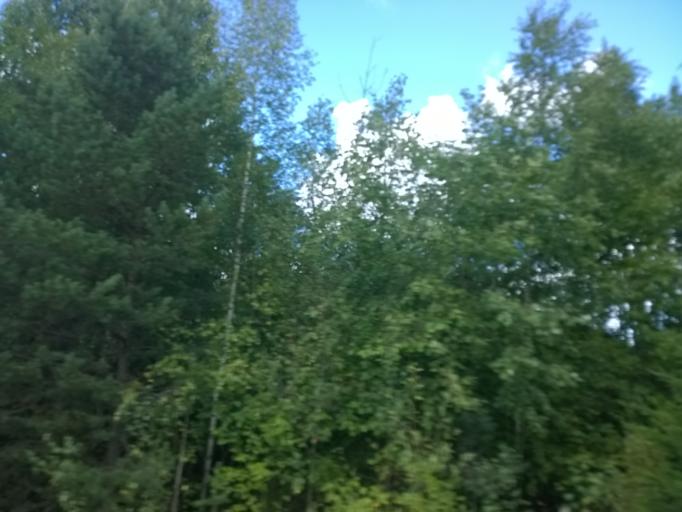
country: FI
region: Pirkanmaa
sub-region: Tampere
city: Tampere
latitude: 61.4532
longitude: 23.8974
